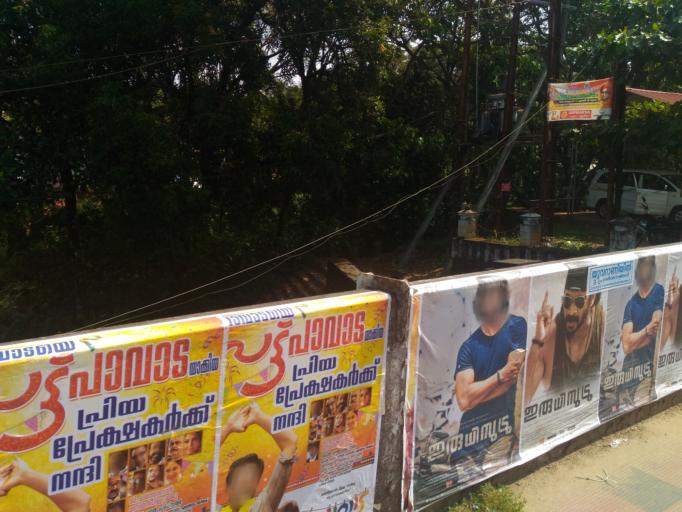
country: IN
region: Kerala
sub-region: Kottayam
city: Lalam
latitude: 9.7105
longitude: 76.6821
